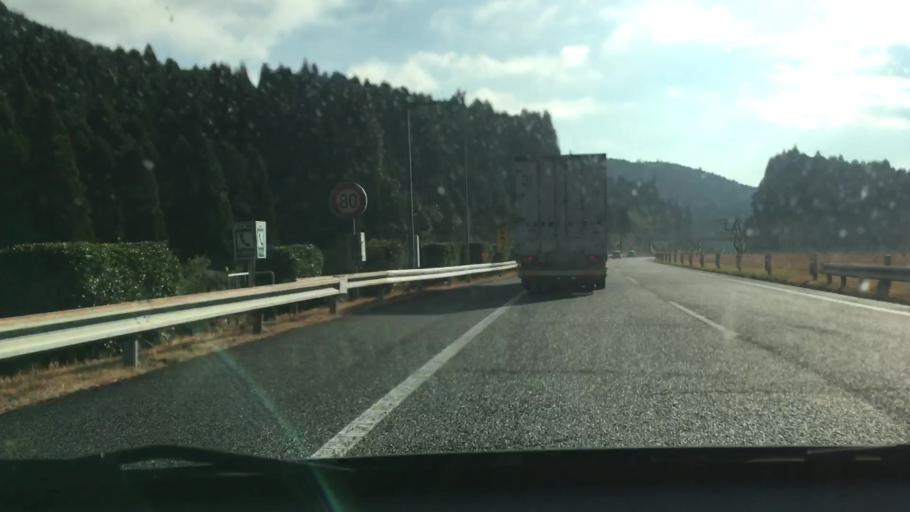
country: JP
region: Kagoshima
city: Okuchi-shinohara
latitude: 31.9648
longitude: 130.7462
